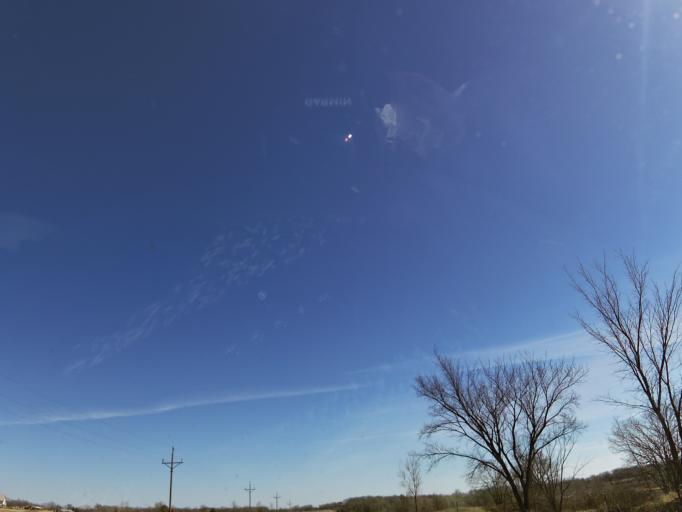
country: US
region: Minnesota
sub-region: Wright County
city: Annandale
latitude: 45.2488
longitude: -94.0895
